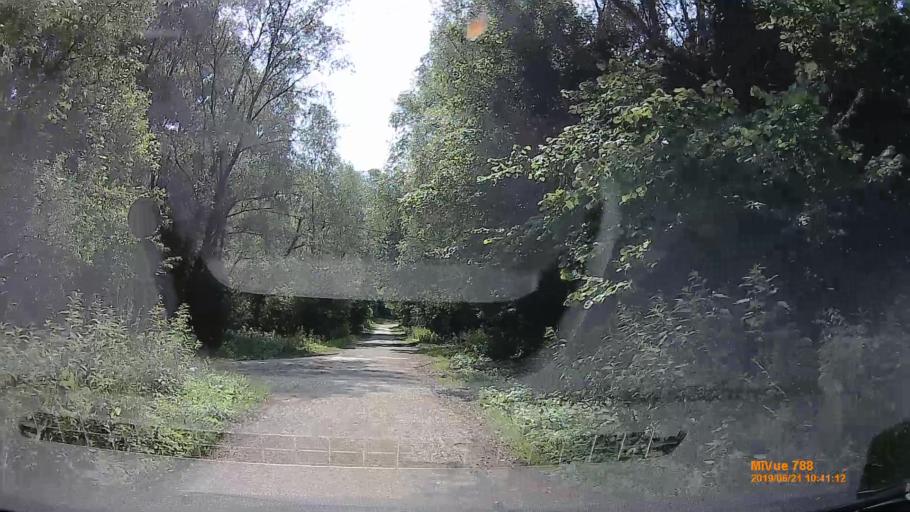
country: HU
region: Baranya
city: Buekkoesd
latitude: 46.1342
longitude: 18.0020
